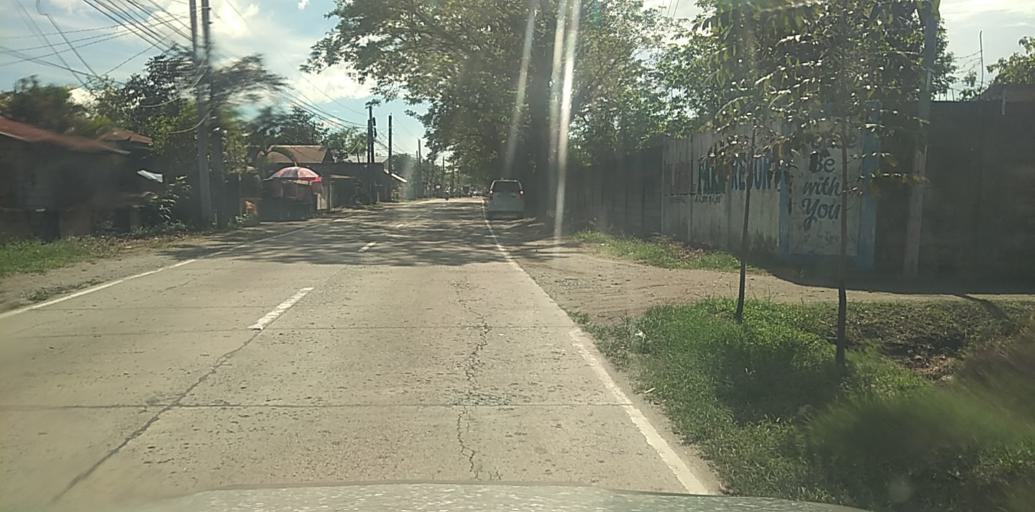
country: PH
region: Central Luzon
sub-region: Province of Pampanga
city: Buensuseso
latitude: 15.1975
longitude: 120.6713
